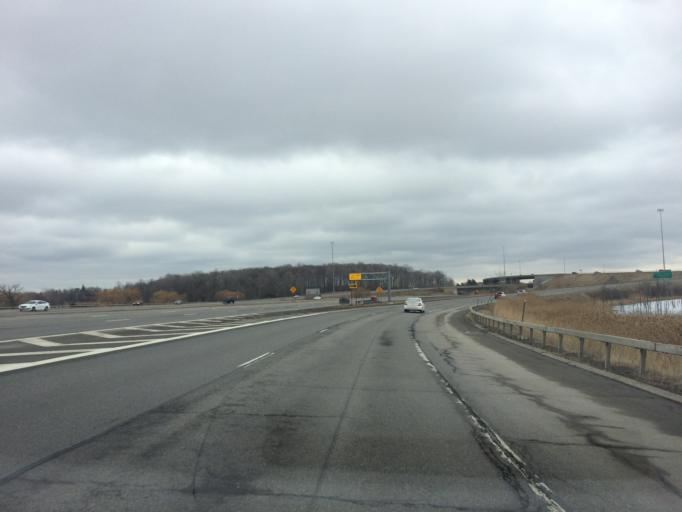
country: US
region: New York
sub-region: Monroe County
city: Rochester
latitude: 43.1099
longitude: -77.6069
